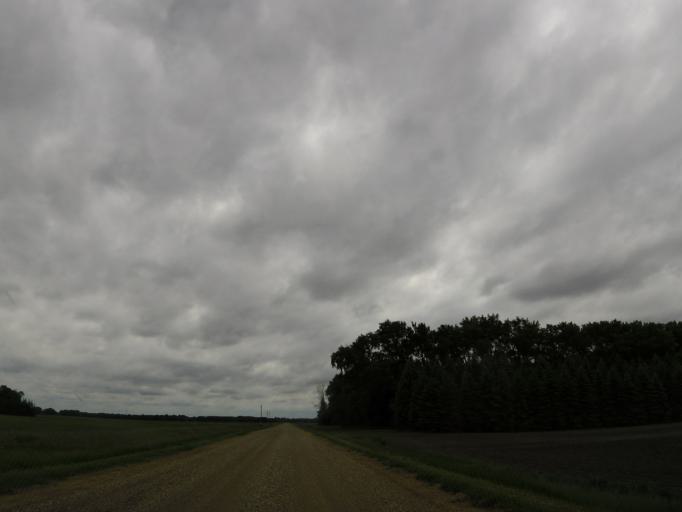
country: US
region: North Dakota
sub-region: Walsh County
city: Grafton
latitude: 48.4656
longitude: -97.5134
